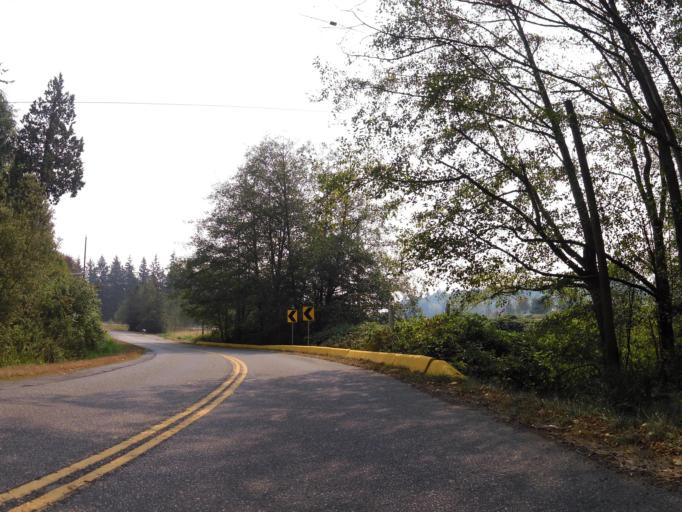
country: US
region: Washington
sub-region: Whatcom County
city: Blaine
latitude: 49.0182
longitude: -122.7573
